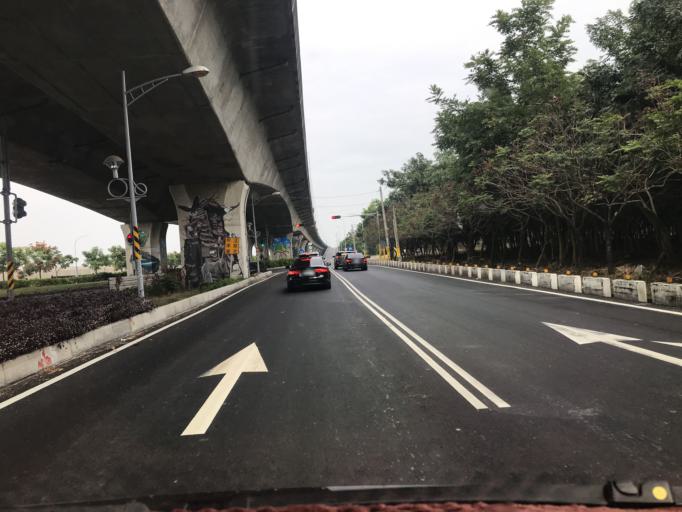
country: TW
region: Taiwan
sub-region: Pingtung
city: Pingtung
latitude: 22.6434
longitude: 120.5406
